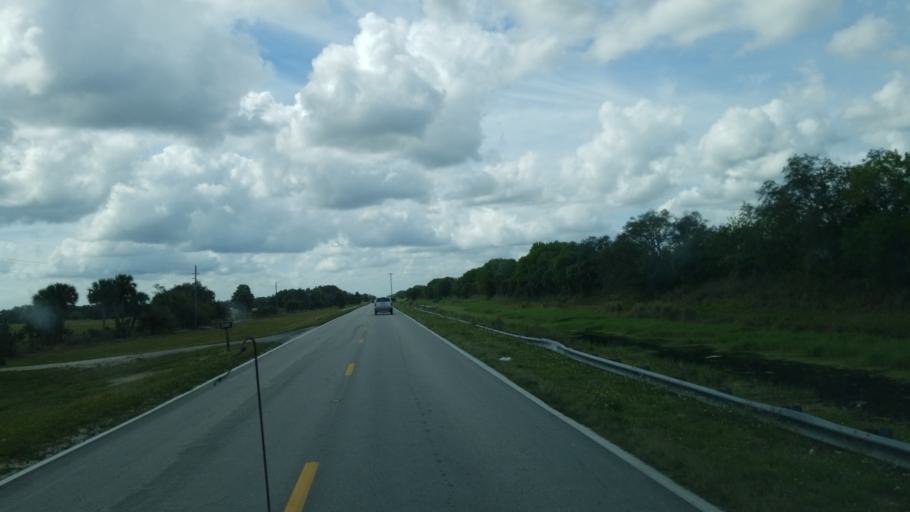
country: US
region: Florida
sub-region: Saint Lucie County
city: Lakewood Park
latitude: 27.4481
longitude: -80.5678
